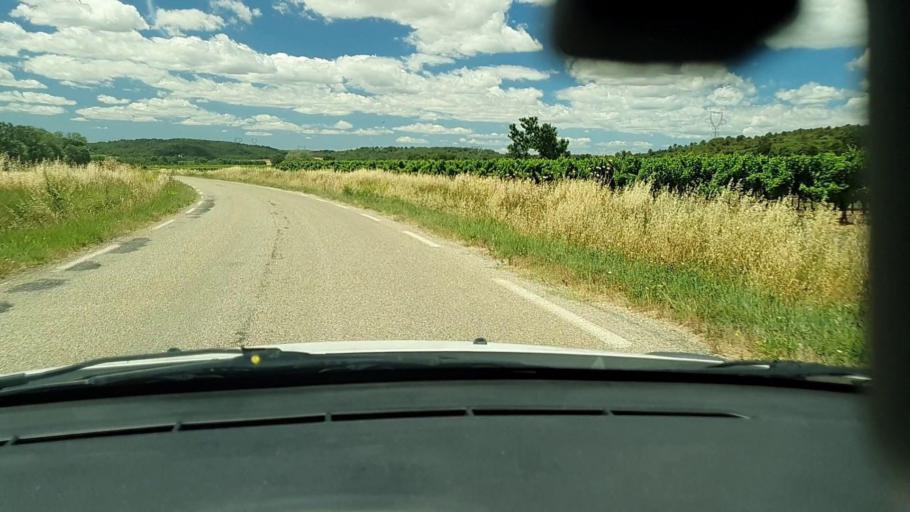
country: FR
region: Languedoc-Roussillon
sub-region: Departement du Gard
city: Blauzac
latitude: 43.9529
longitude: 4.4061
